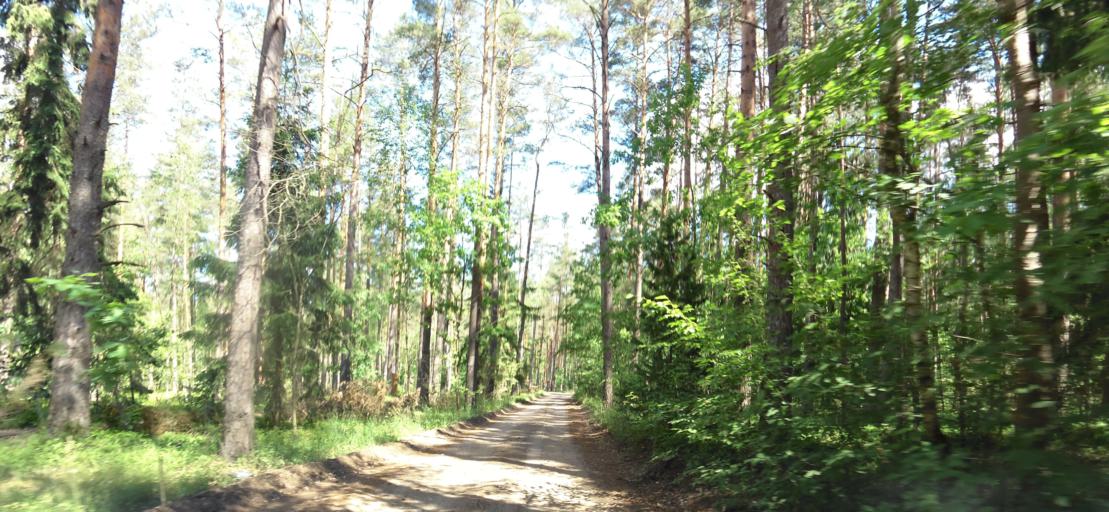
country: LT
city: Nemencine
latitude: 54.8160
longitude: 25.3885
